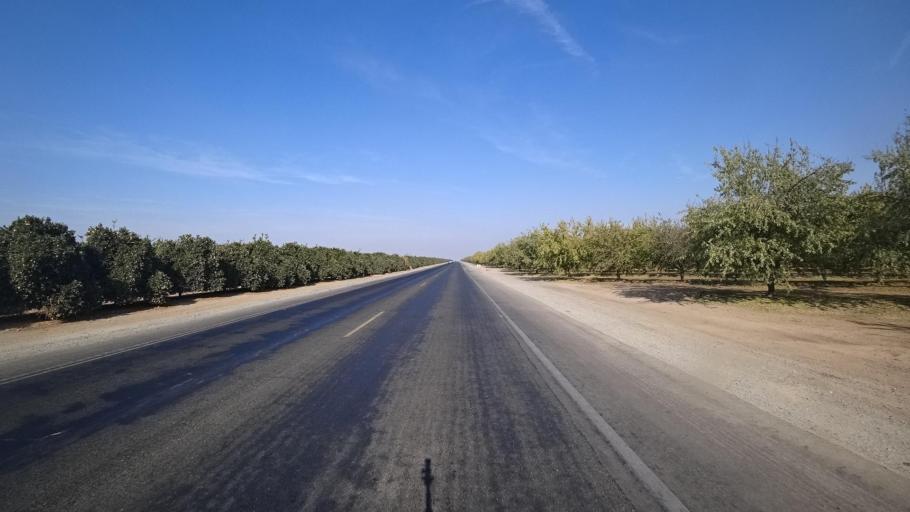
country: US
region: California
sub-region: Kern County
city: McFarland
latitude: 35.6932
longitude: -119.1750
